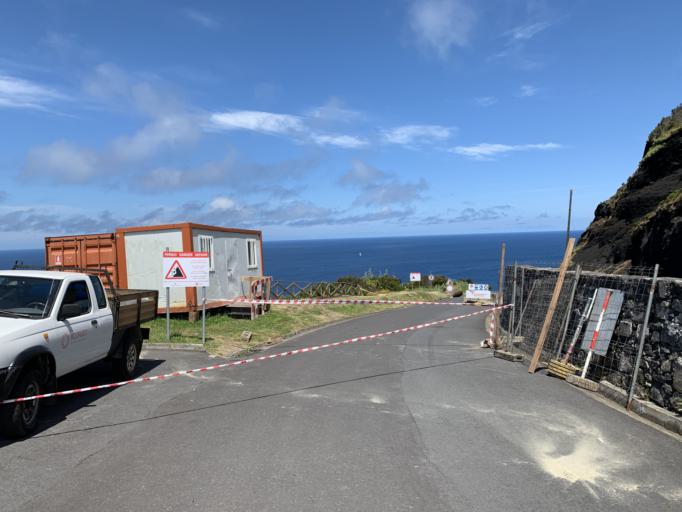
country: PT
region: Azores
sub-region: Ponta Delgada
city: Arrifes
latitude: 37.8580
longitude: -25.8505
